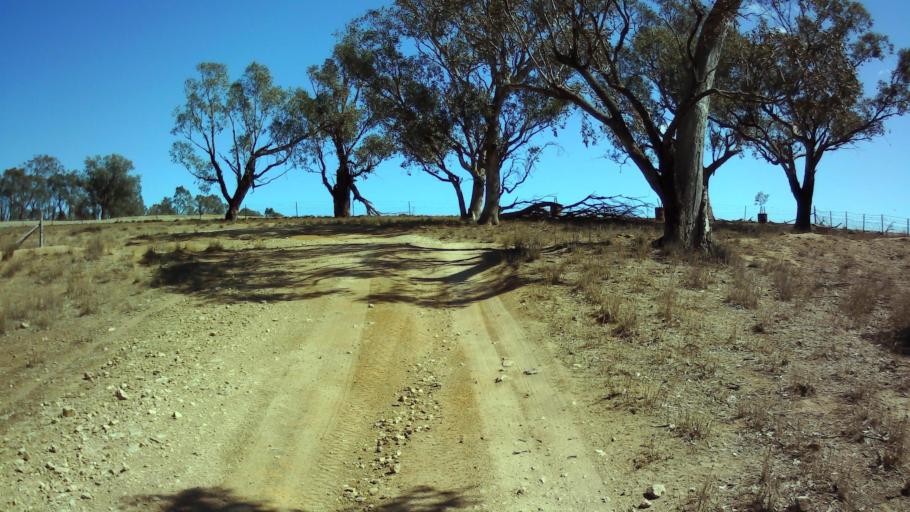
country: AU
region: New South Wales
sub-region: Weddin
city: Grenfell
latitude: -33.9966
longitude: 148.4373
